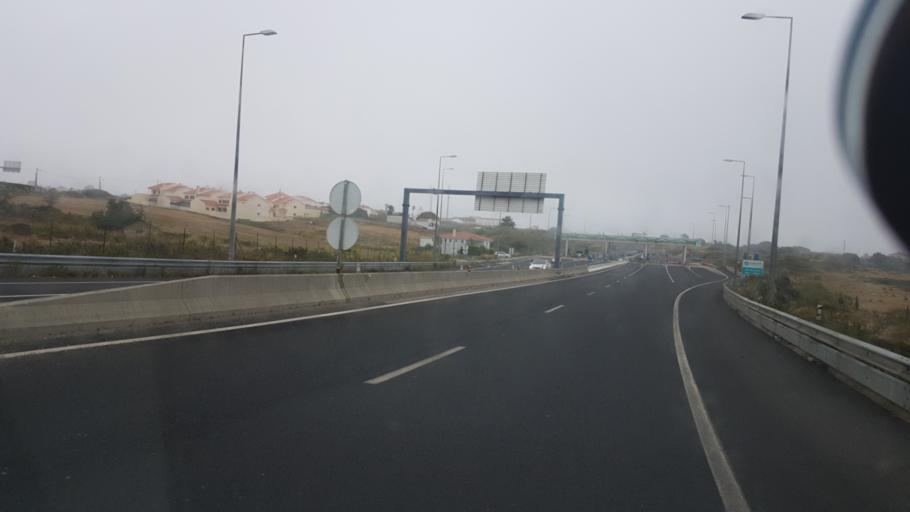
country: PT
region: Lisbon
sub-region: Mafra
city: Ericeira
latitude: 38.9646
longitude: -9.4053
